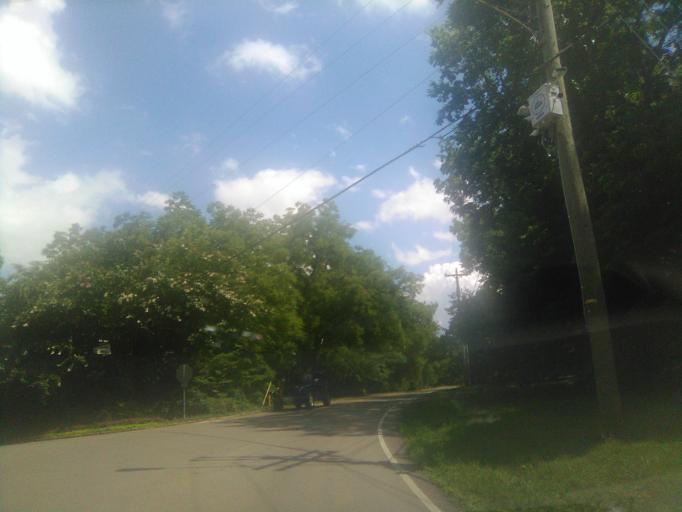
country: US
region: Tennessee
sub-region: Davidson County
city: Belle Meade
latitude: 36.1107
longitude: -86.8451
